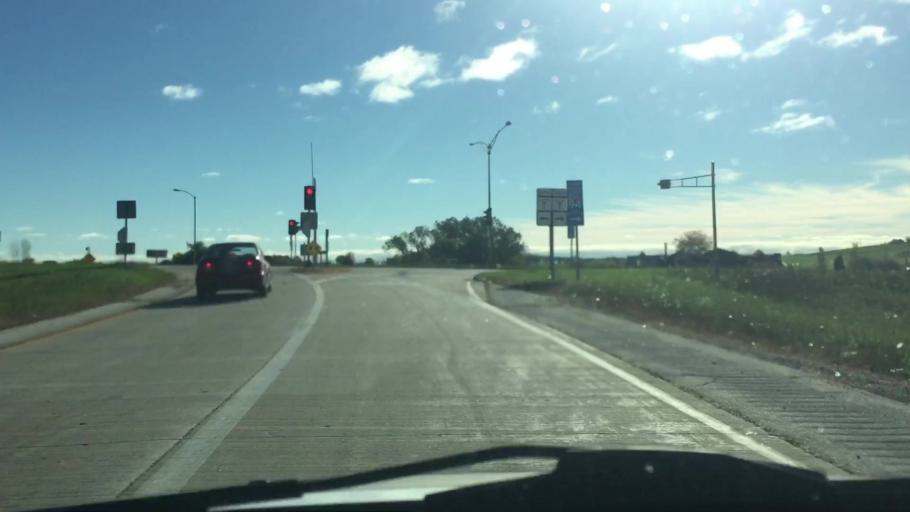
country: US
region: Wisconsin
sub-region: Waukesha County
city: Pewaukee
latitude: 43.0459
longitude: -88.2567
